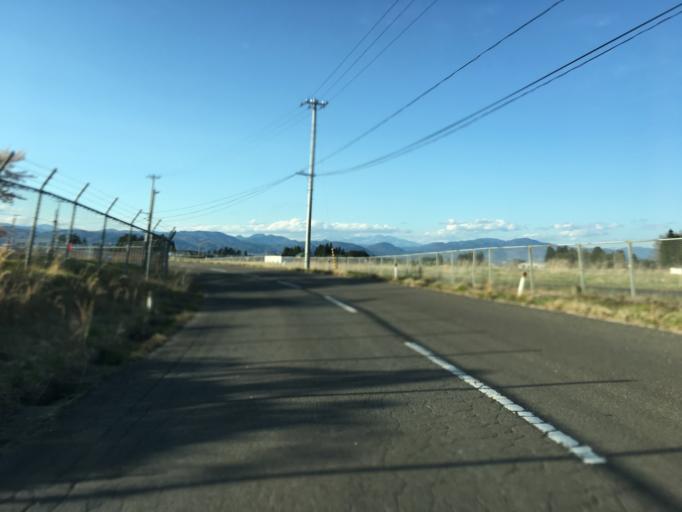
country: JP
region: Fukushima
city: Fukushima-shi
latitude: 37.7102
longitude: 140.3874
